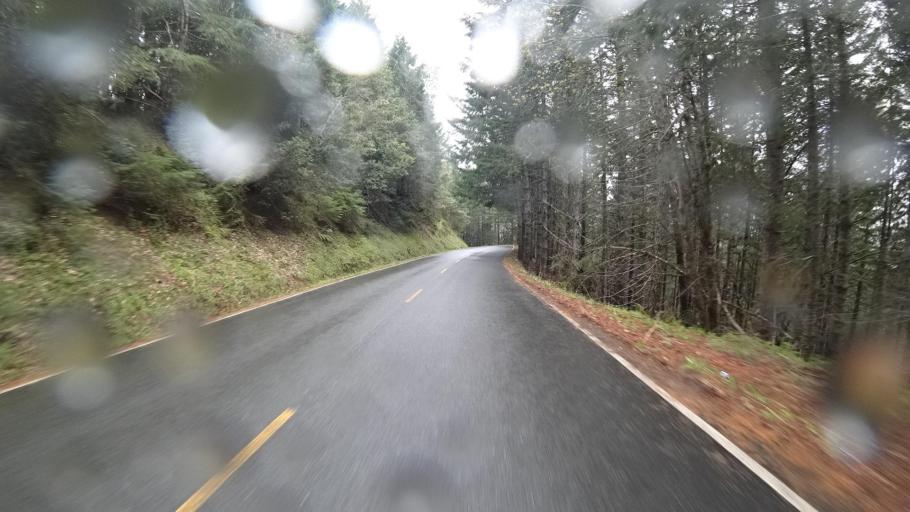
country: US
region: California
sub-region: Humboldt County
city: Westhaven-Moonstone
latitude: 41.1478
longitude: -123.8408
